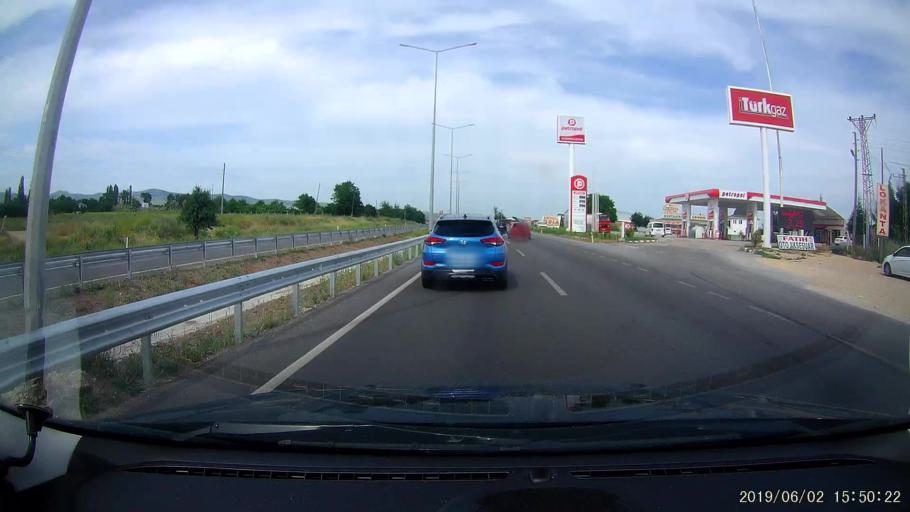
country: TR
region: Amasya
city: Merzifon
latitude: 40.8592
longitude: 35.4796
